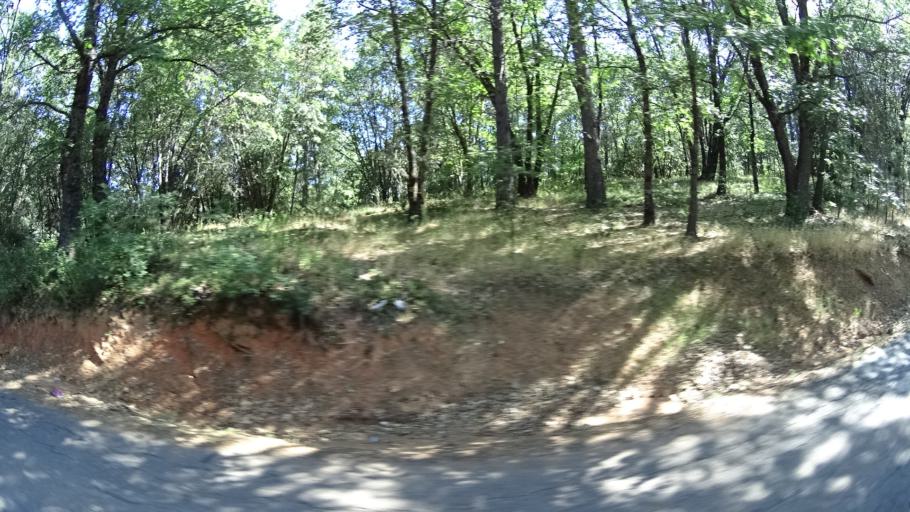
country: US
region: California
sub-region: Amador County
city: Pioneer
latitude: 38.3989
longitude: -120.5155
